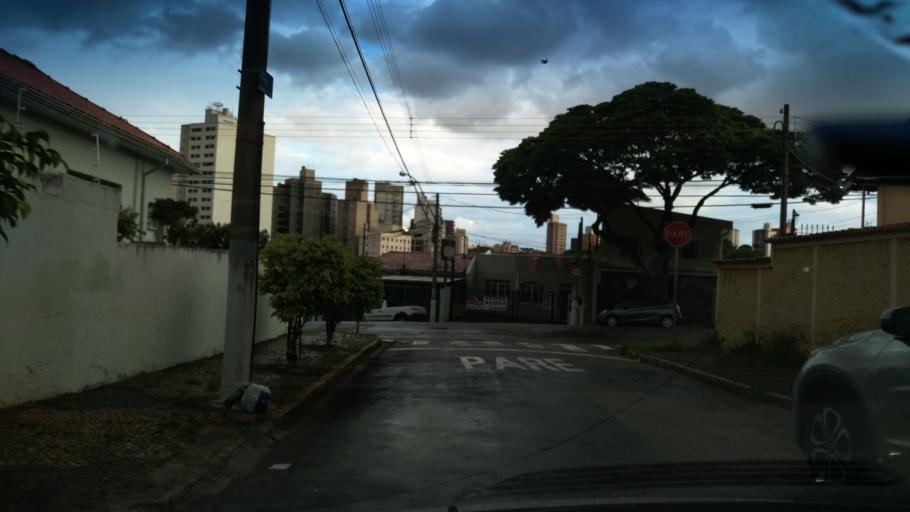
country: BR
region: Sao Paulo
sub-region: Campinas
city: Campinas
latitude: -22.9106
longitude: -47.0472
